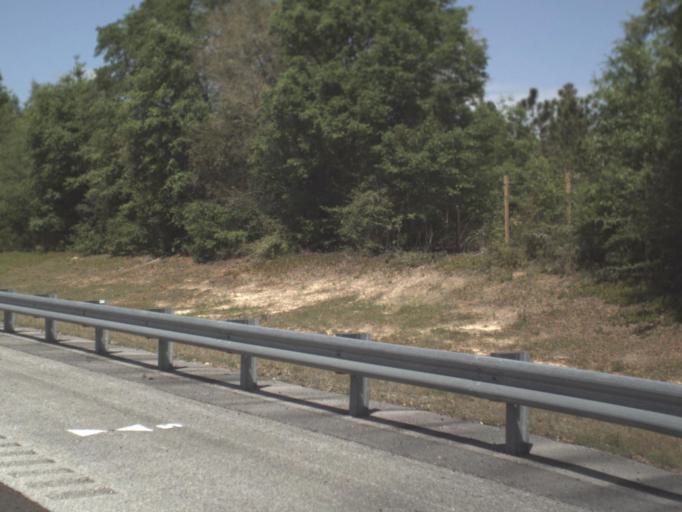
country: US
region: Florida
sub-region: Santa Rosa County
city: East Milton
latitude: 30.6244
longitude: -86.9467
